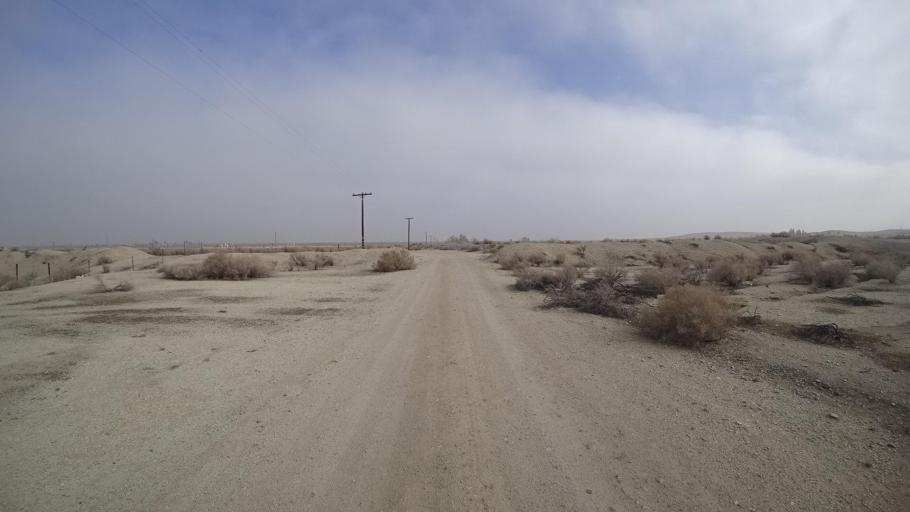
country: US
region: California
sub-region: Kern County
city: Maricopa
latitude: 35.0472
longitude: -119.3650
